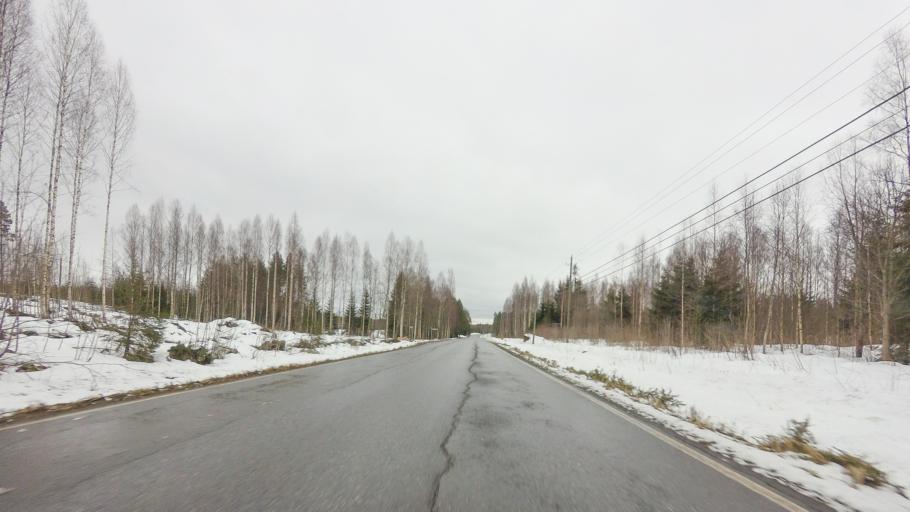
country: FI
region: Southern Savonia
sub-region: Savonlinna
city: Savonlinna
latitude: 61.9478
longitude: 28.8643
